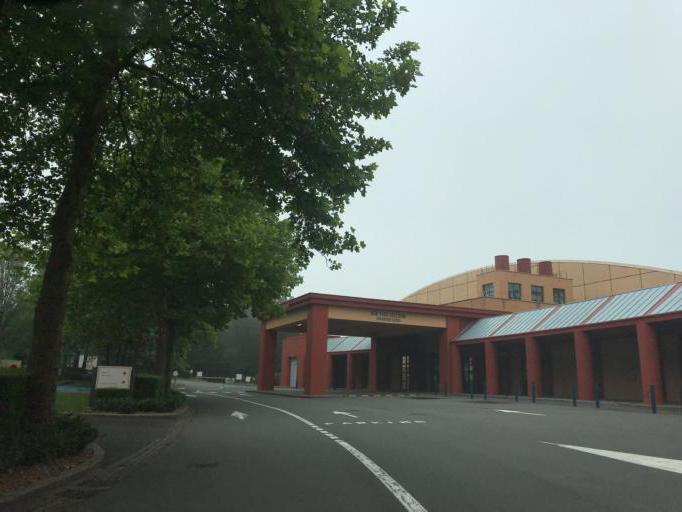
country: FR
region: Ile-de-France
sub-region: Departement de Seine-et-Marne
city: Coupvray
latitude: 48.8708
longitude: 2.7877
